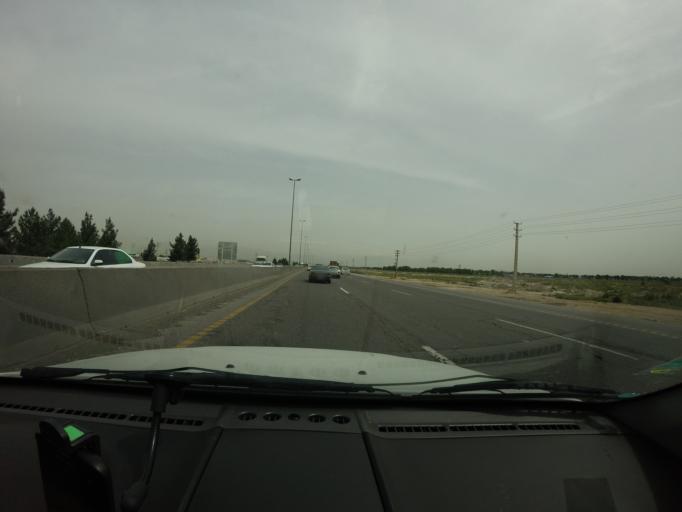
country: IR
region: Tehran
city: Robat Karim
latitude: 35.5578
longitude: 51.1286
